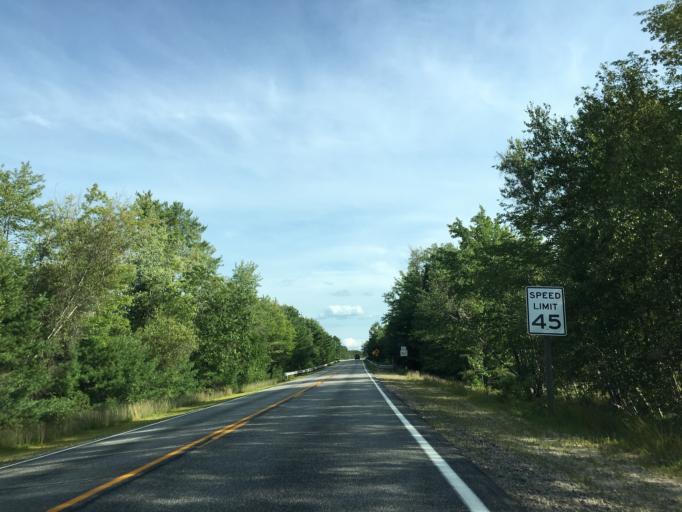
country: US
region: Maine
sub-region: Oxford County
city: Brownfield
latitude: 43.9479
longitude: -70.8901
